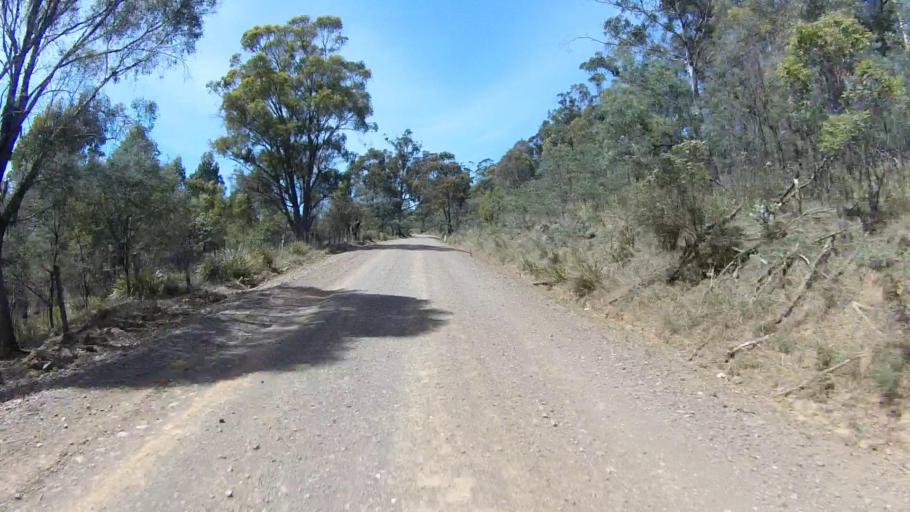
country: AU
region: Tasmania
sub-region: Sorell
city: Sorell
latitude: -42.6472
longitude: 147.7426
